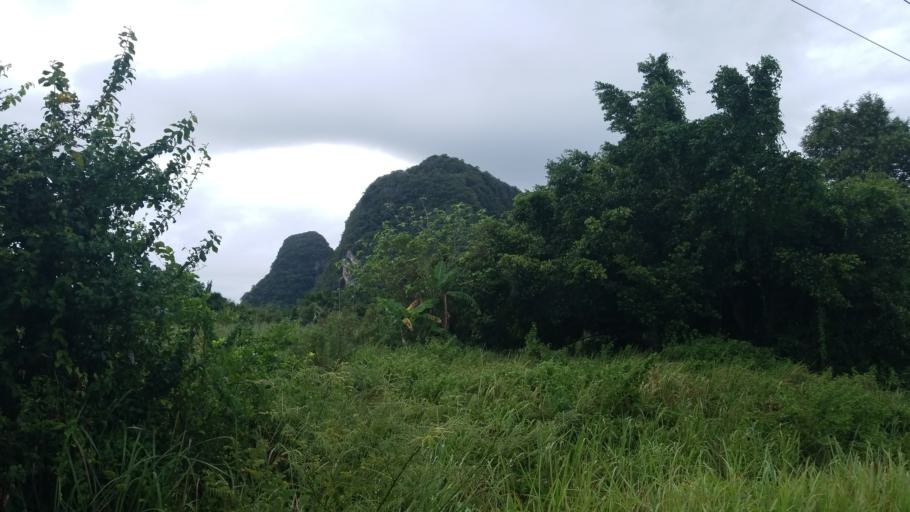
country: TH
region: Krabi
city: Nuea Khlong
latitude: 7.9698
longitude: 98.9841
